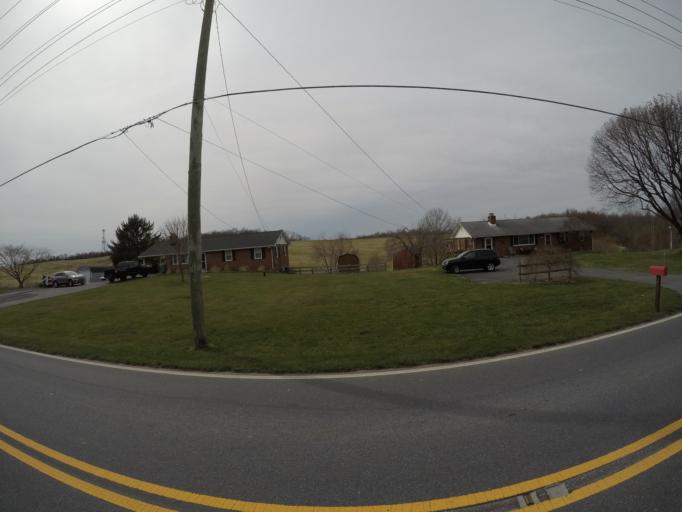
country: US
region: Maryland
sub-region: Frederick County
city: Green Valley
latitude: 39.3570
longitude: -77.2697
